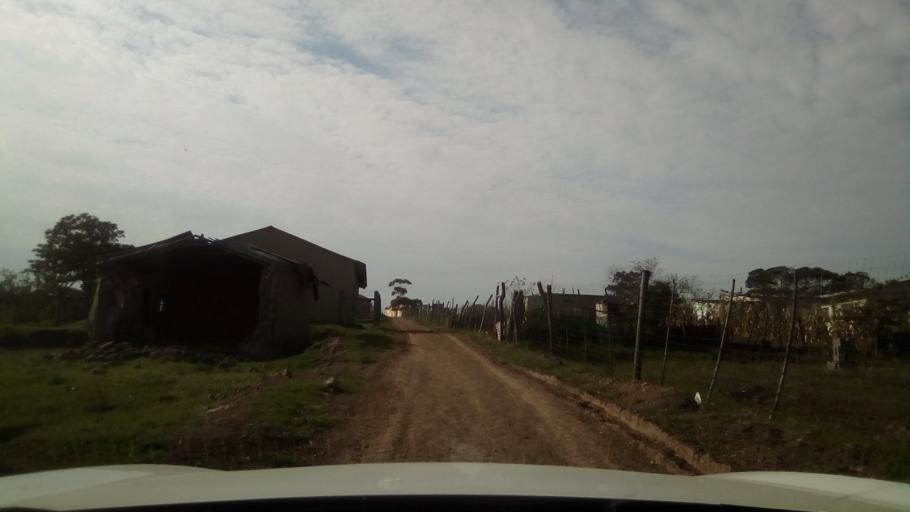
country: ZA
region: Eastern Cape
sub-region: Buffalo City Metropolitan Municipality
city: Bhisho
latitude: -33.0095
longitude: 27.3051
